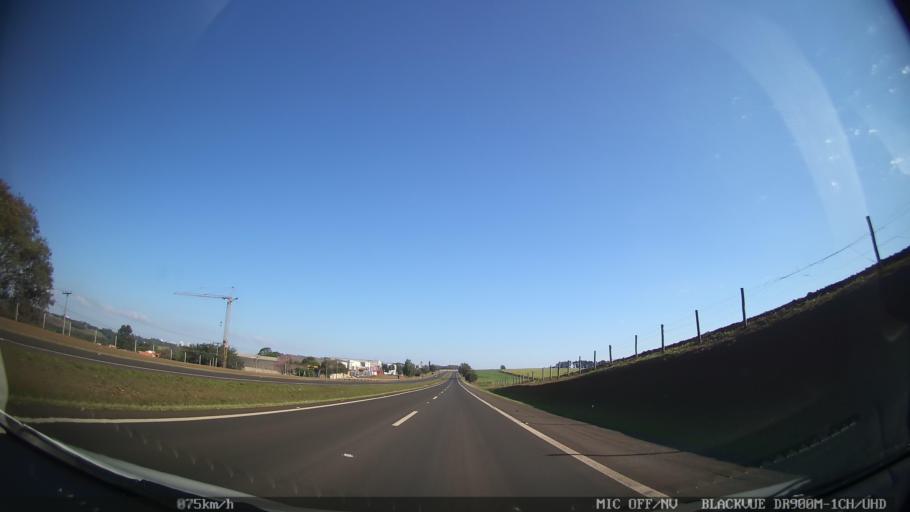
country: BR
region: Sao Paulo
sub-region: Piracicaba
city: Piracicaba
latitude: -22.6809
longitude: -47.6363
